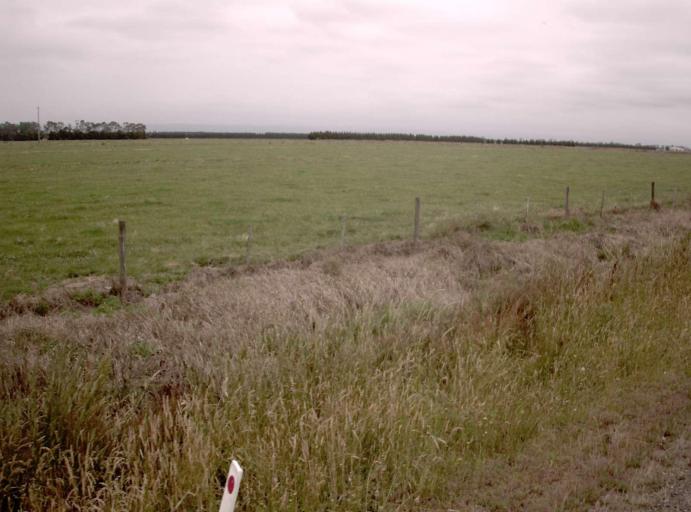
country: AU
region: Victoria
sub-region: Wellington
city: Heyfield
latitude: -38.0927
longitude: 146.7726
